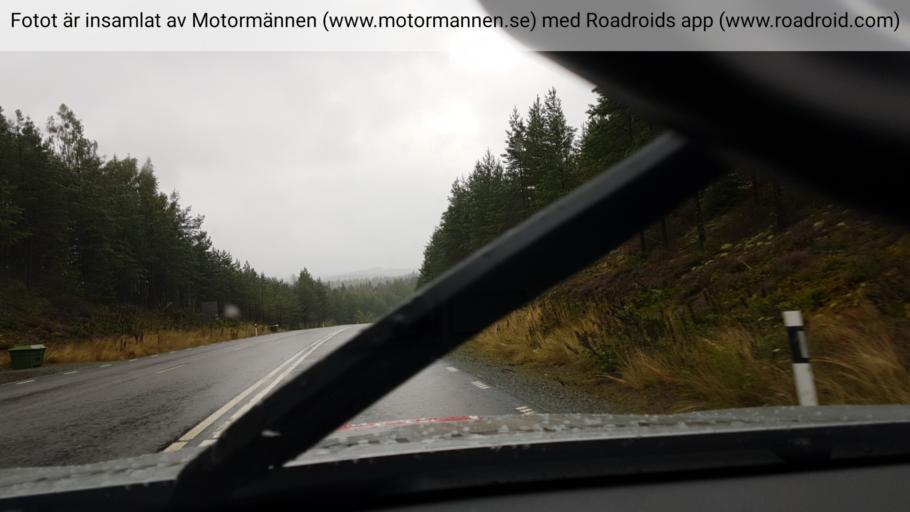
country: SE
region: Vaestra Goetaland
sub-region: Bengtsfors Kommun
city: Dals Langed
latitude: 58.8495
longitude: 12.1680
